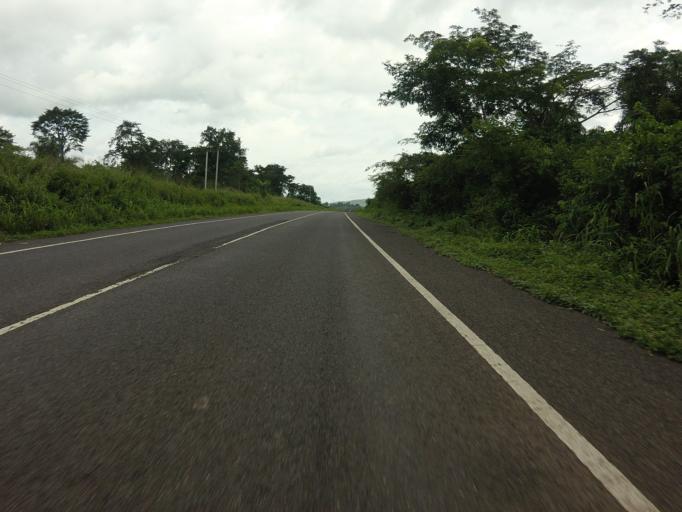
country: TG
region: Plateaux
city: Badou
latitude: 7.9798
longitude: 0.5604
